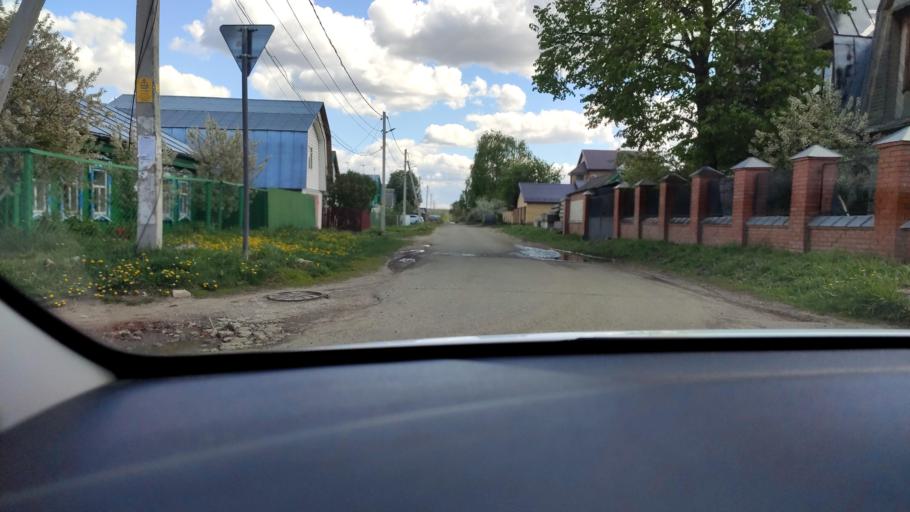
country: RU
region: Tatarstan
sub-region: Gorod Kazan'
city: Kazan
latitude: 55.7046
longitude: 49.1486
